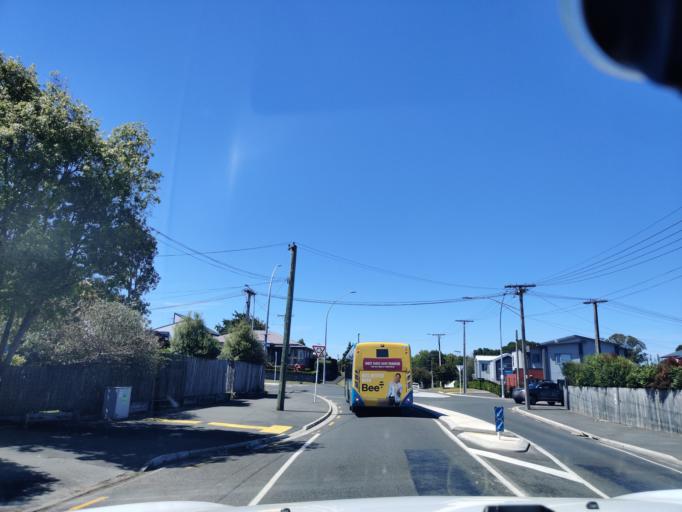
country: NZ
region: Waikato
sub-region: Hamilton City
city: Hamilton
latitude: -37.7944
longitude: 175.2675
